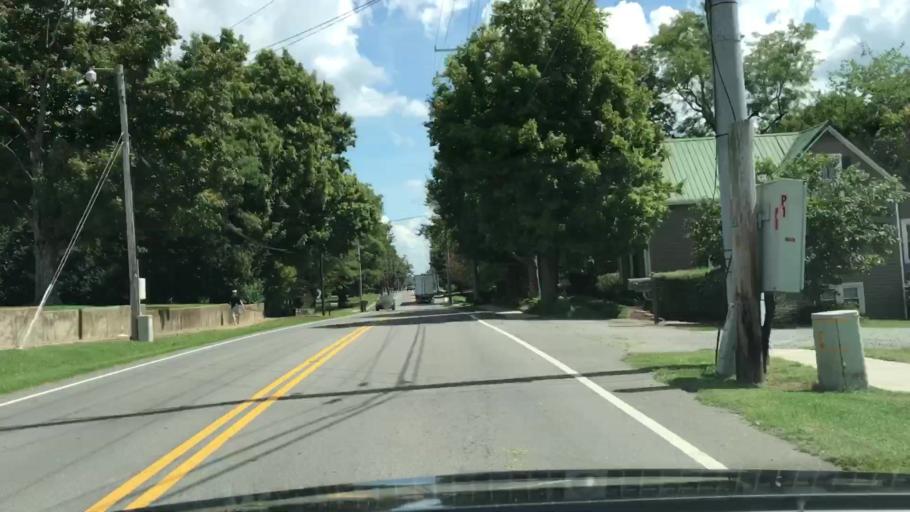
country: US
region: Tennessee
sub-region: Robertson County
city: Cross Plains
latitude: 36.5490
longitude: -86.7023
